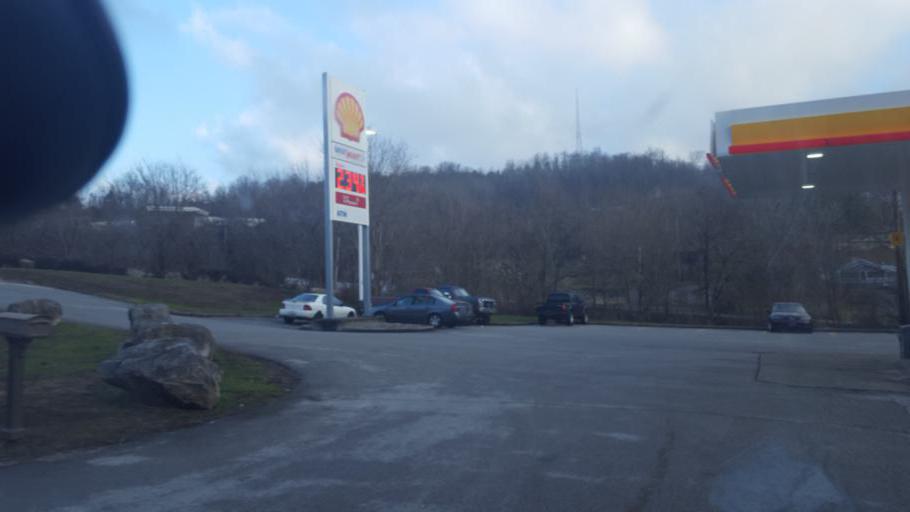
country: US
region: Kentucky
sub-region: Rockcastle County
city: Mount Vernon
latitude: 37.3412
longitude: -84.3055
